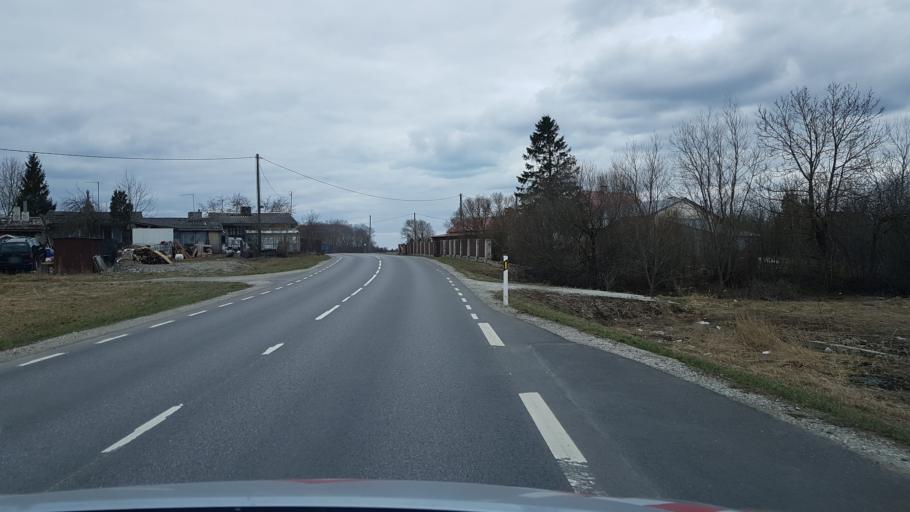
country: EE
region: Ida-Virumaa
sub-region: Narva-Joesuu linn
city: Narva-Joesuu
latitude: 59.4026
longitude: 28.0655
